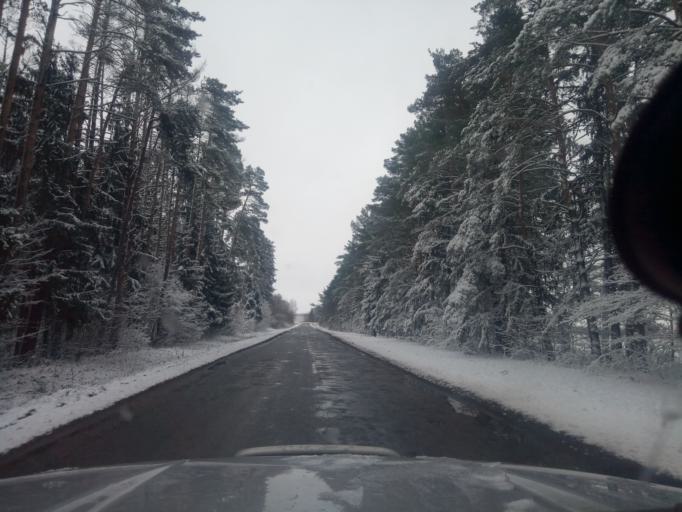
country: BY
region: Minsk
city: Tsimkavichy
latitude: 53.0531
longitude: 26.8924
